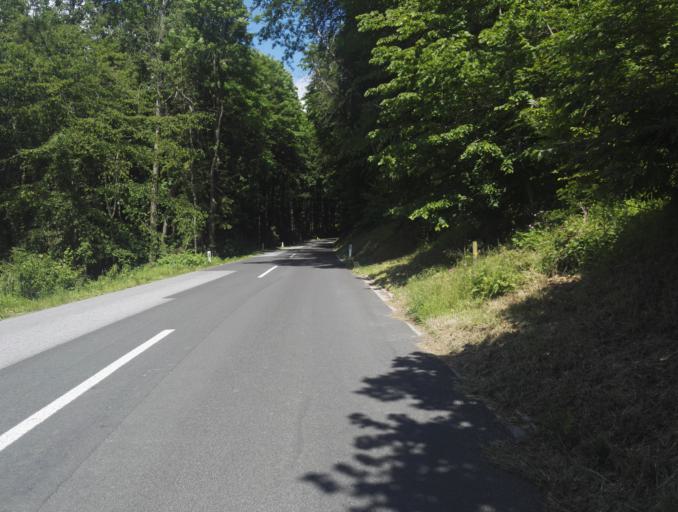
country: AT
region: Styria
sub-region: Politischer Bezirk Graz-Umgebung
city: Deutschfeistritz
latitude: 47.2160
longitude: 15.3091
